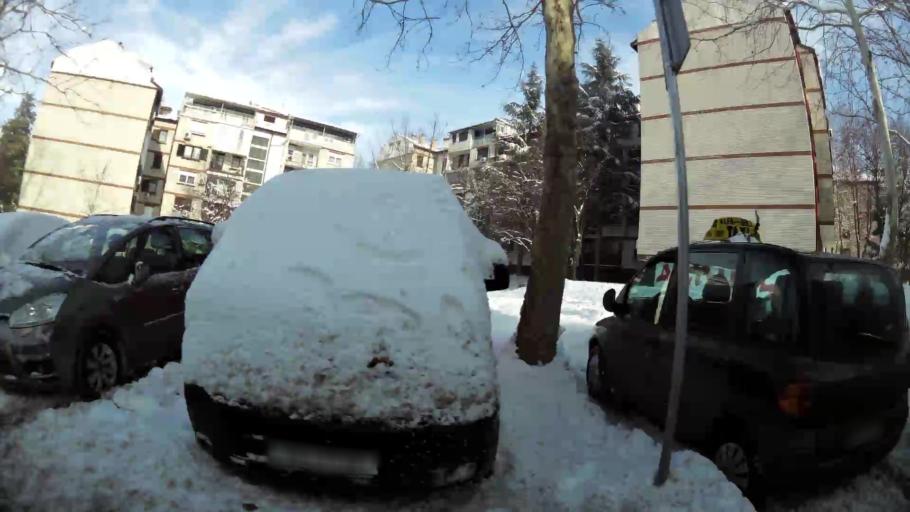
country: RS
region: Central Serbia
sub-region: Belgrade
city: Zvezdara
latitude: 44.7886
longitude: 20.5440
